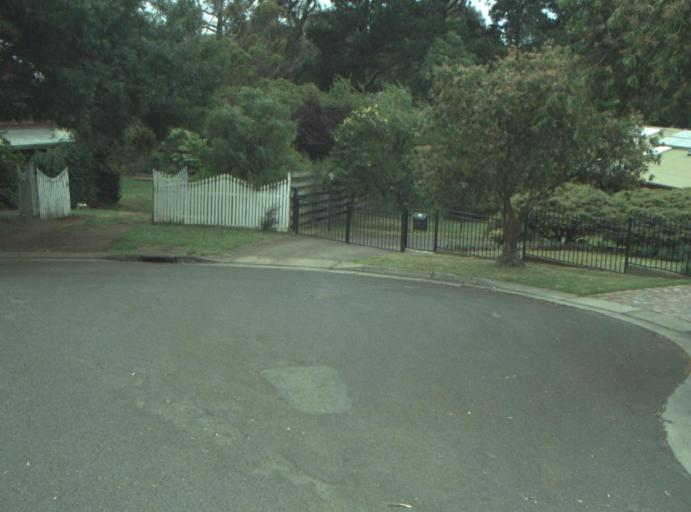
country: AU
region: Victoria
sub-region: Greater Geelong
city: Wandana Heights
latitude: -38.1930
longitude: 144.3276
